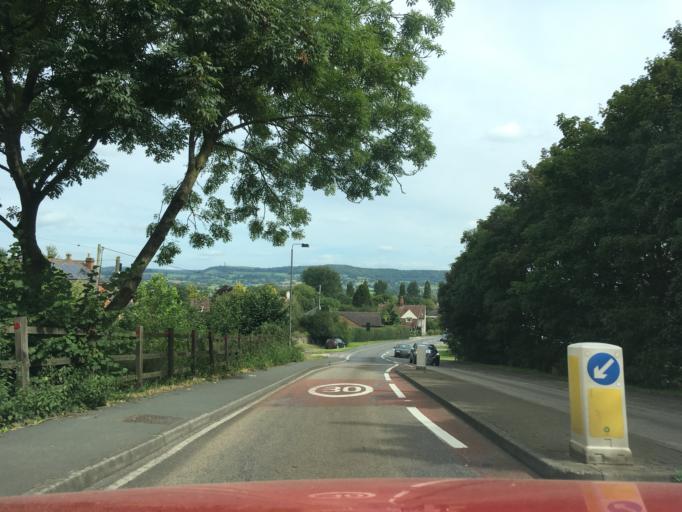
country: GB
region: England
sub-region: South Gloucestershire
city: Charfield
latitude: 51.6263
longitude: -2.4107
